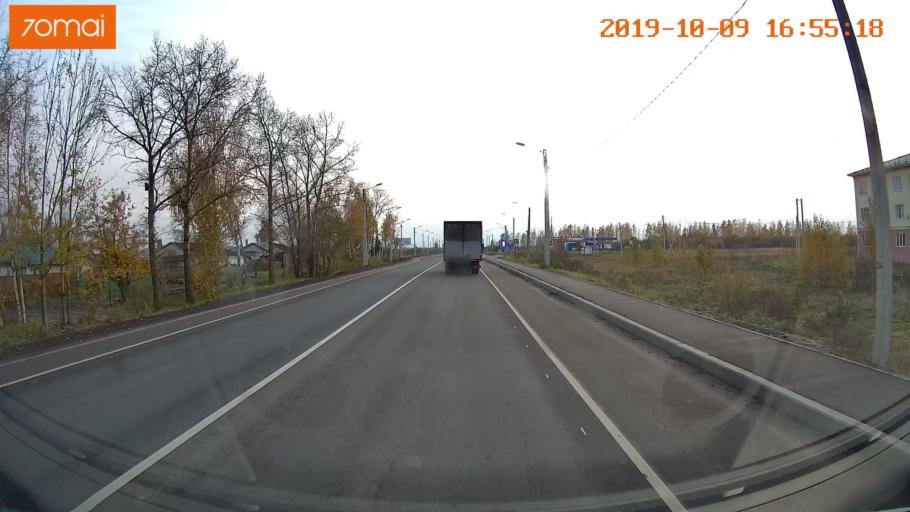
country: RU
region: Ivanovo
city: Privolzhsk
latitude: 57.3687
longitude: 41.2747
